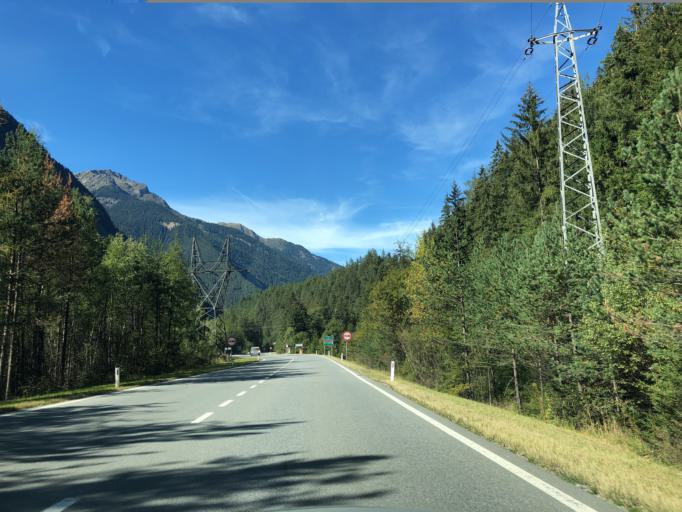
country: AT
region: Tyrol
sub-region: Politischer Bezirk Imst
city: Umhausen
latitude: 47.1214
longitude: 10.9316
